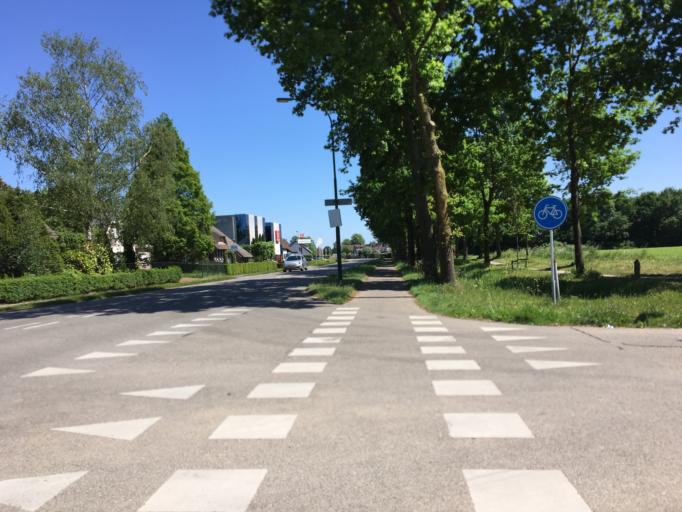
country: NL
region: Gelderland
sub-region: Gemeente Zaltbommel
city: Nederhemert-Noord
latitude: 51.7508
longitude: 5.2099
